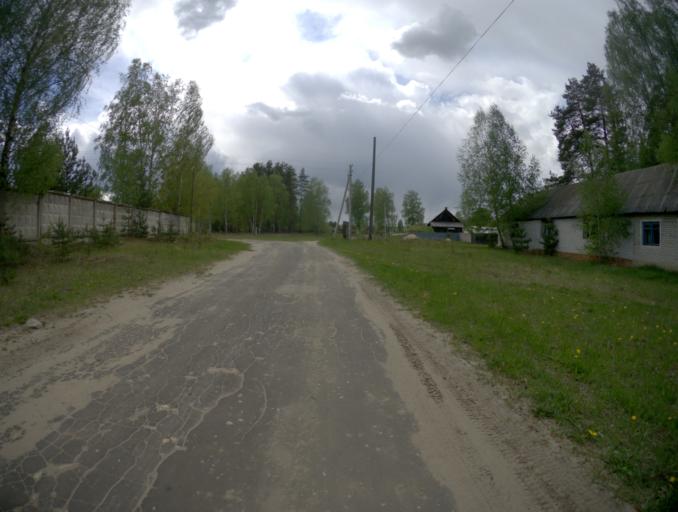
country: RU
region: Vladimir
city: Velikodvorskiy
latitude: 55.2379
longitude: 40.6509
